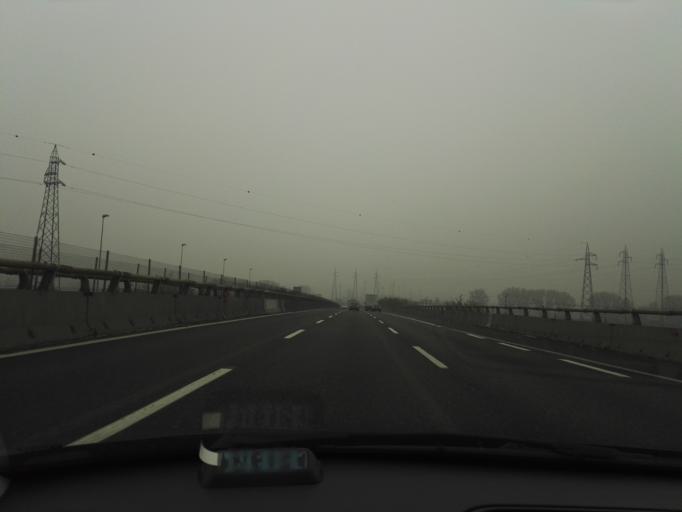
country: IT
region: Lombardy
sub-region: Citta metropolitana di Milano
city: Chiaravalle
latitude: 45.4229
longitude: 9.2456
